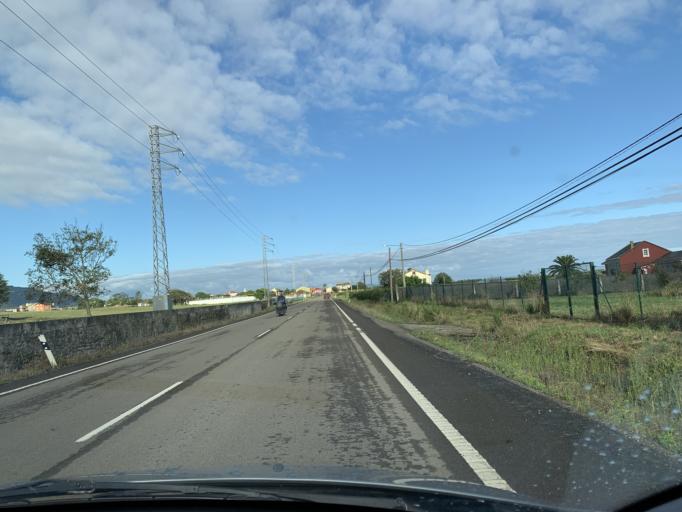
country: ES
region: Galicia
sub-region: Provincia de Lugo
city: Ribadeo
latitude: 43.5444
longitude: -7.0826
